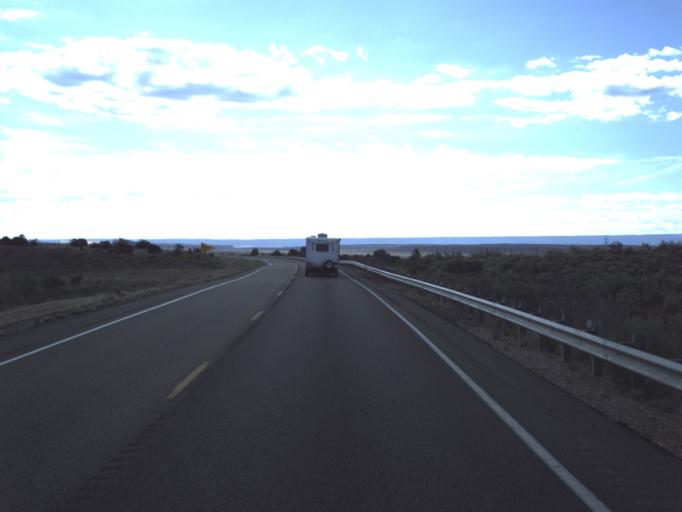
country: US
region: Utah
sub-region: Kane County
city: Kanab
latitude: 37.0305
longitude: -112.4906
